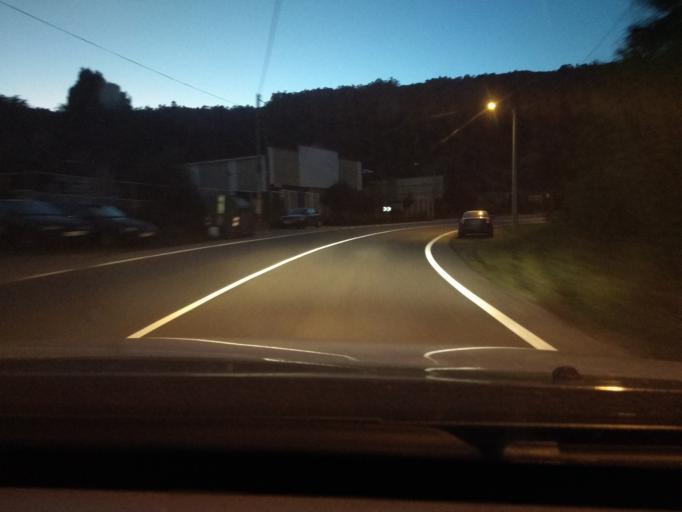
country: ES
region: Galicia
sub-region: Provincia de Pontevedra
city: Moana
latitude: 42.2894
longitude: -8.7433
